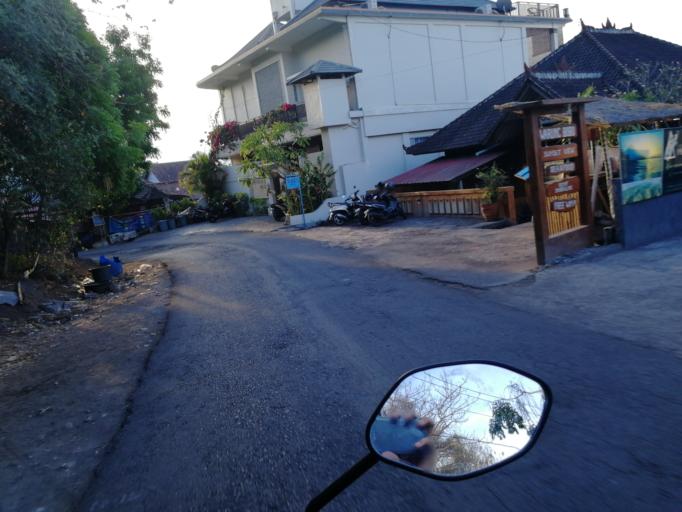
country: ID
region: Bali
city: Biaslantang Kaler
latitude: -8.3351
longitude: 115.6536
